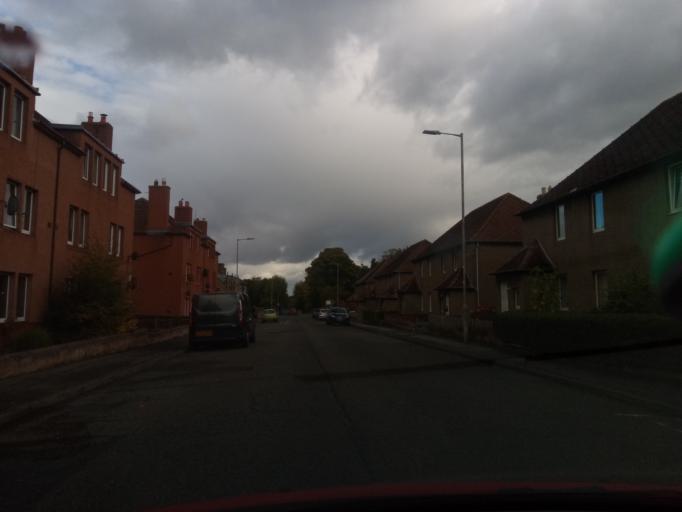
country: GB
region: Scotland
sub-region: The Scottish Borders
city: Galashiels
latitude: 55.6077
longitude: -2.7899
